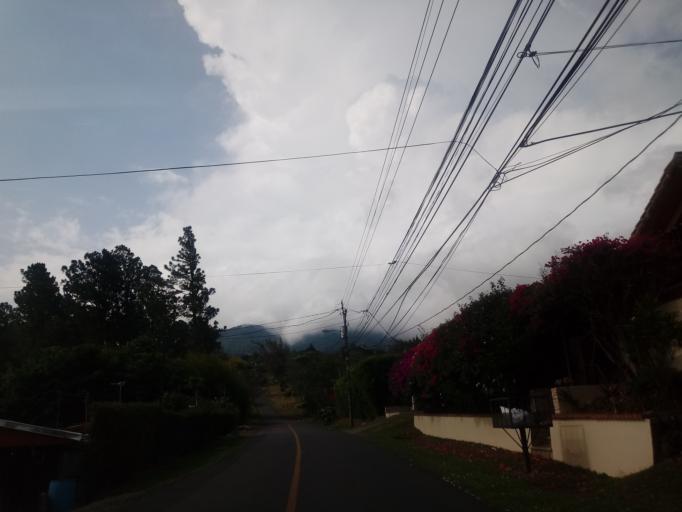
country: CR
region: Heredia
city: Angeles
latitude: 10.0284
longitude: -84.0442
